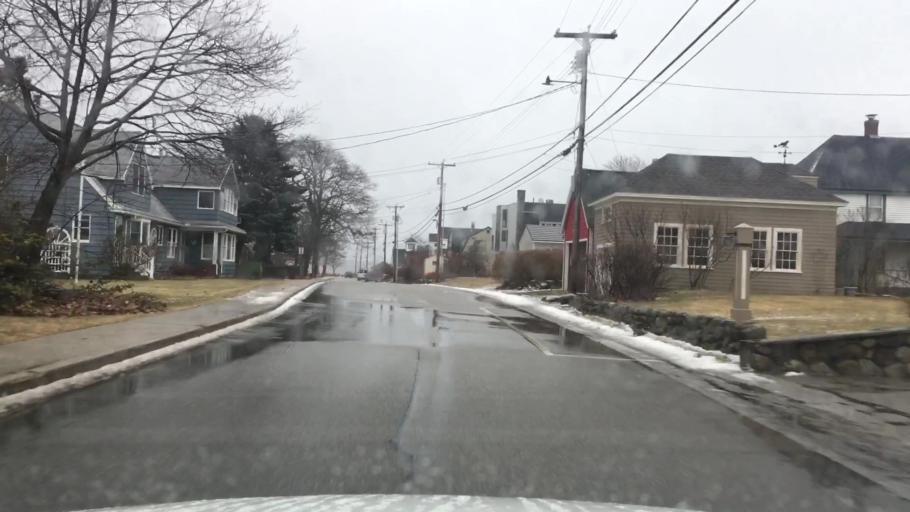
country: US
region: Maine
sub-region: York County
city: Arundel
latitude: 43.3984
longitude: -70.4151
